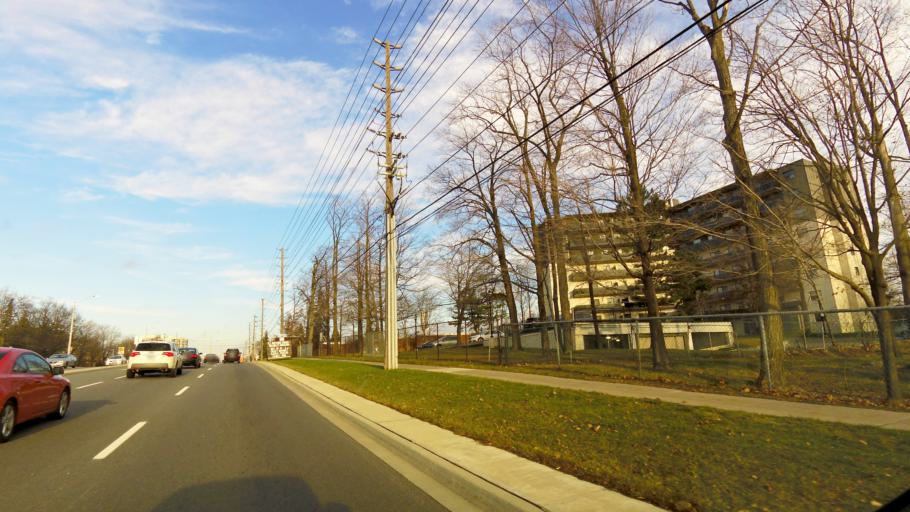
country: CA
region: Ontario
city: Etobicoke
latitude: 43.6205
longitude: -79.6046
